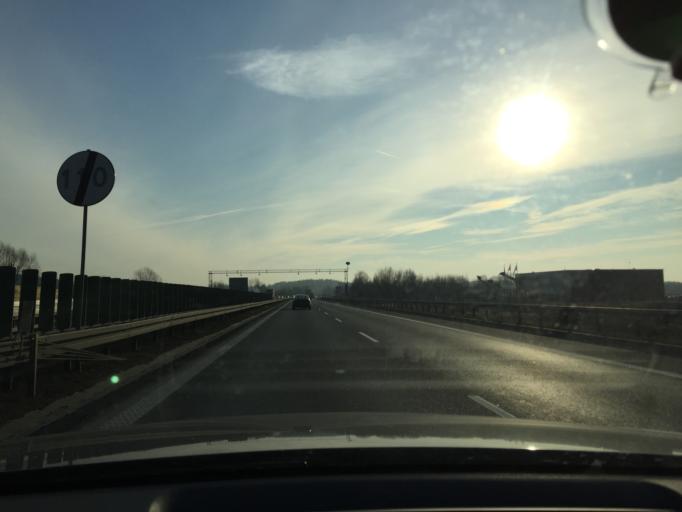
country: PL
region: Lesser Poland Voivodeship
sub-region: Powiat krakowski
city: Kryspinow
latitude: 50.0590
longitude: 19.8096
